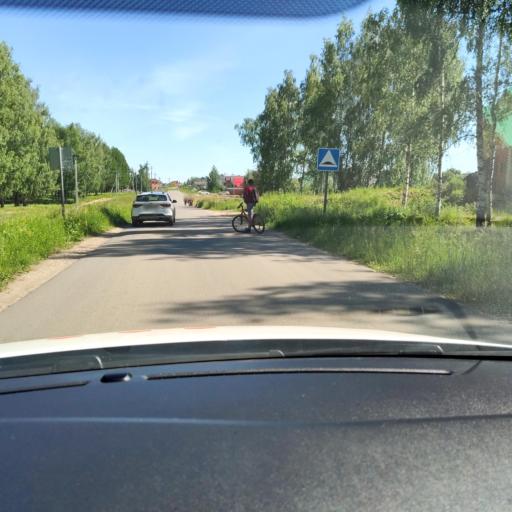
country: RU
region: Tatarstan
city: Staroye Arakchino
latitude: 55.8878
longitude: 49.0358
